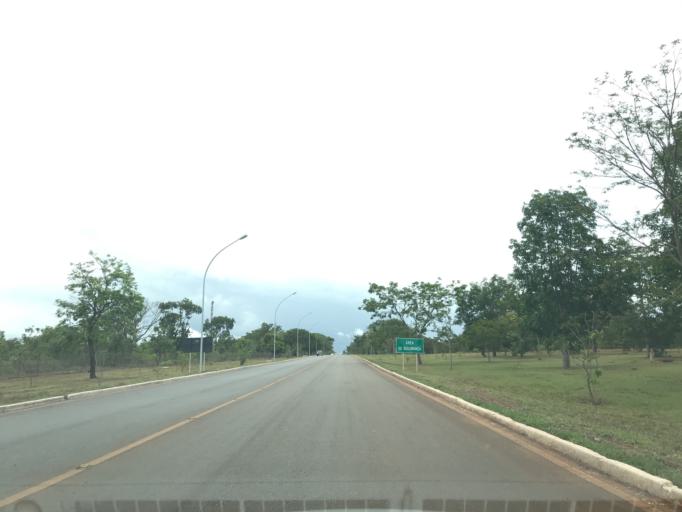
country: BR
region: Federal District
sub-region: Brasilia
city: Brasilia
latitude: -15.7978
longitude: -47.8422
